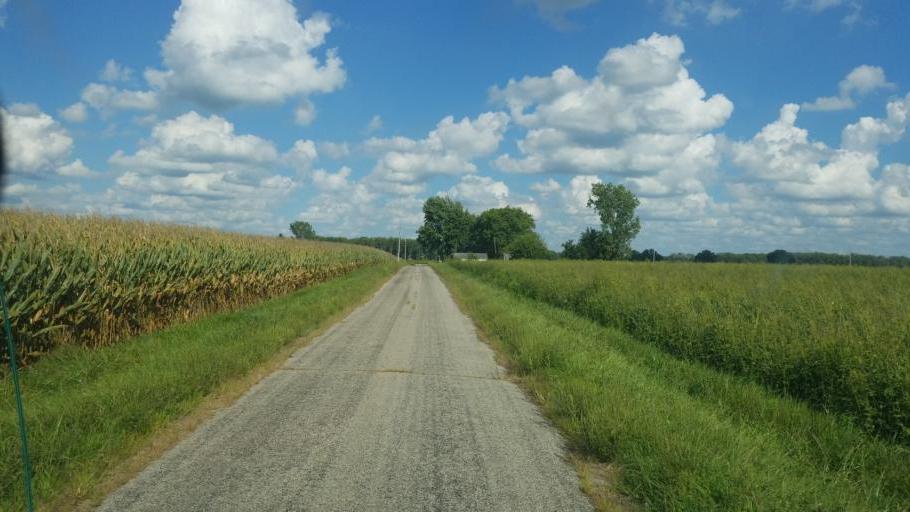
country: US
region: Ohio
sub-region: Union County
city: Richwood
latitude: 40.4662
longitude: -83.3297
